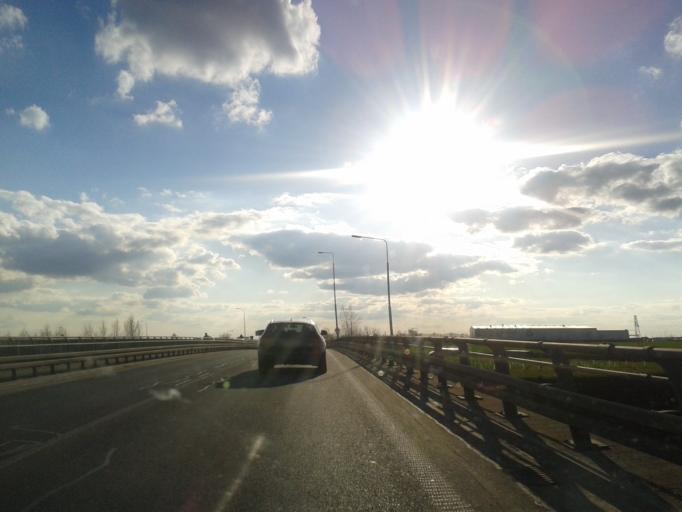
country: CZ
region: Central Bohemia
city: Hostivice
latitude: 50.0532
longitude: 14.2774
